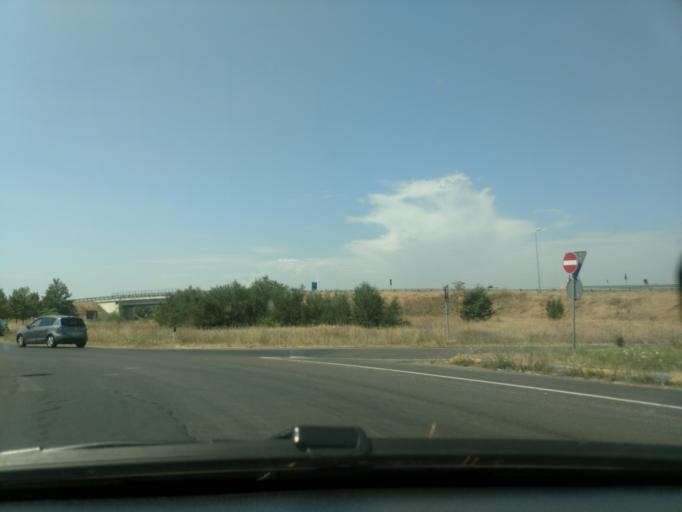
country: IT
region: Emilia-Romagna
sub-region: Provincia di Bologna
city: Medicina-Buda
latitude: 44.4418
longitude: 11.6086
